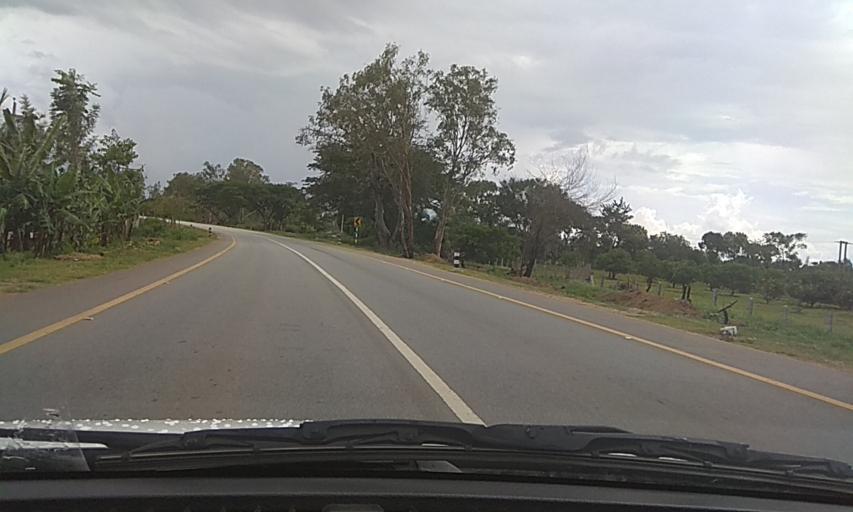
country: IN
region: Karnataka
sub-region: Tumkur
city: Kunigal
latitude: 12.9157
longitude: 77.0324
